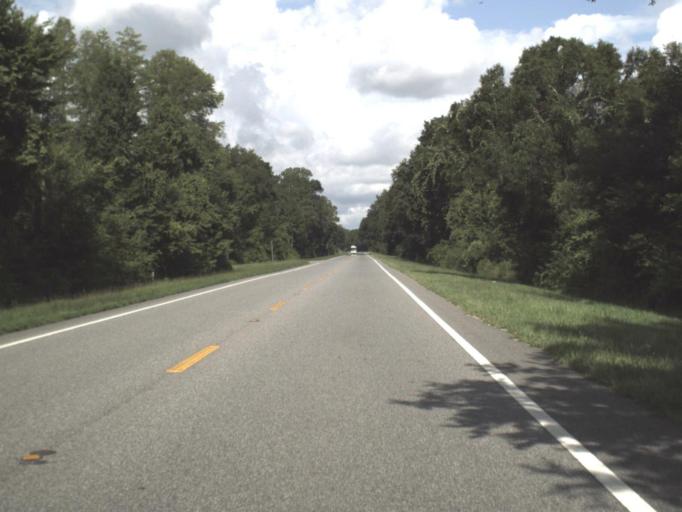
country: US
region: Florida
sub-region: Hernando County
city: Ridge Manor
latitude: 28.5077
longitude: -82.1411
